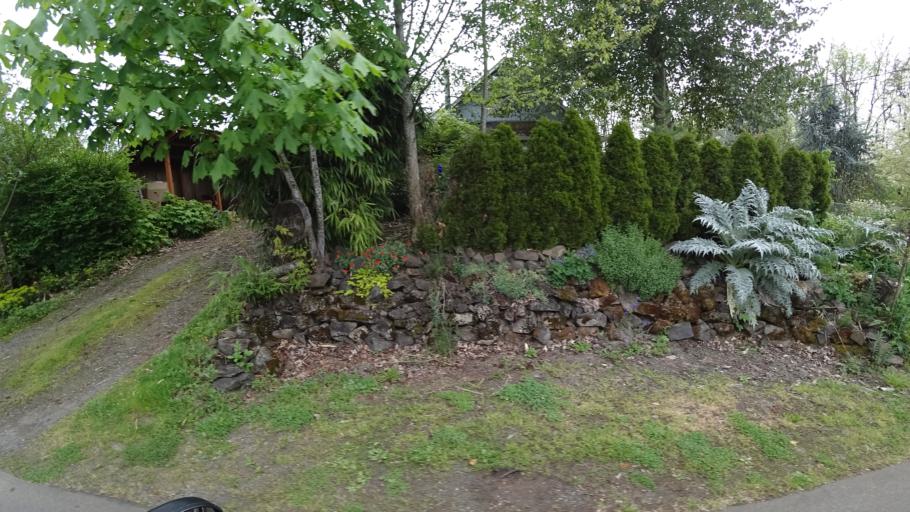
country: US
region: Oregon
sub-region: Washington County
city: Hillsboro
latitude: 45.5447
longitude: -122.9990
